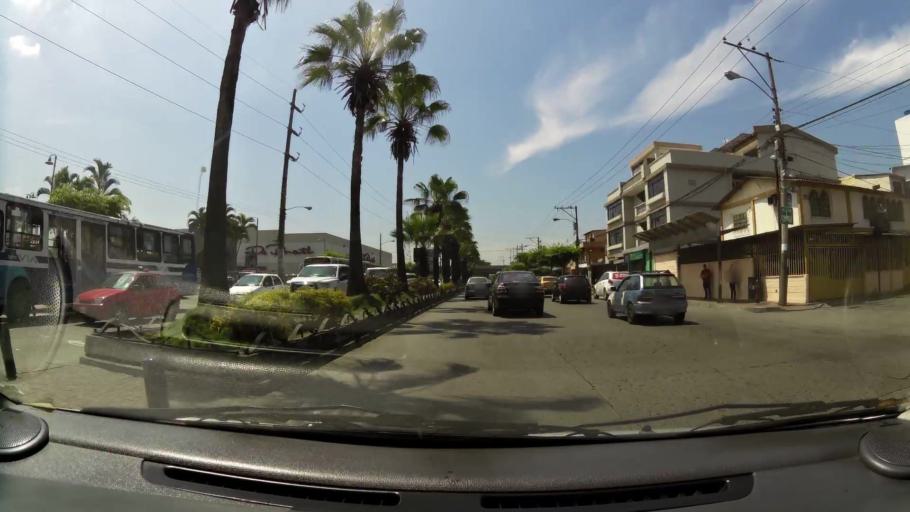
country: EC
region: Guayas
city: Eloy Alfaro
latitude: -2.1396
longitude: -79.9075
